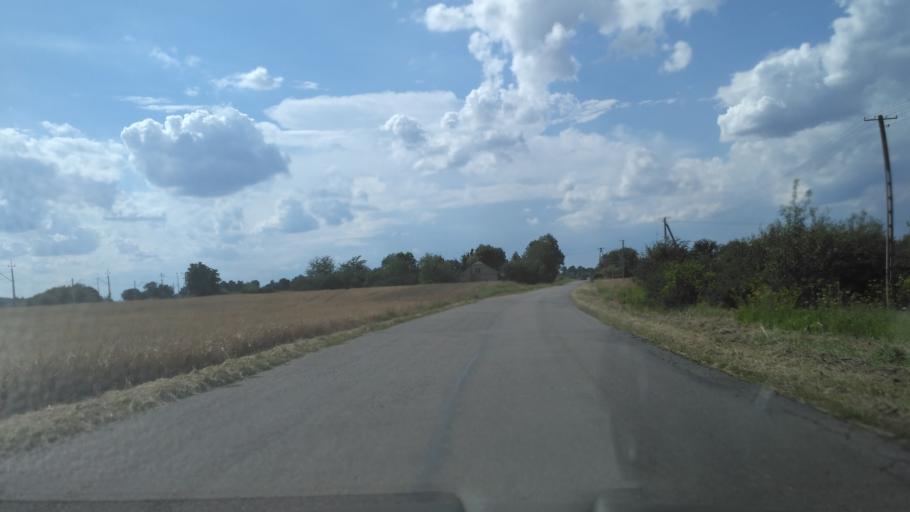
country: PL
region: Lublin Voivodeship
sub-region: Powiat leczynski
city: Milejow
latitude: 51.2104
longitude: 22.8755
